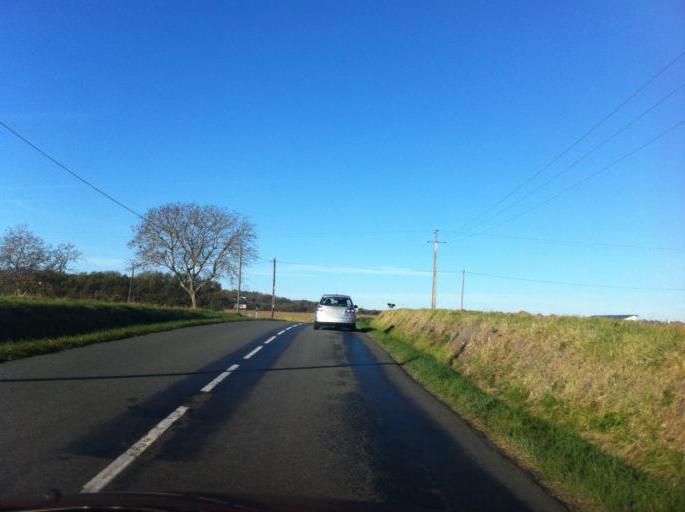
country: FR
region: Aquitaine
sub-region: Departement de la Dordogne
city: Saint-Aulaye
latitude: 45.2606
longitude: 0.1930
